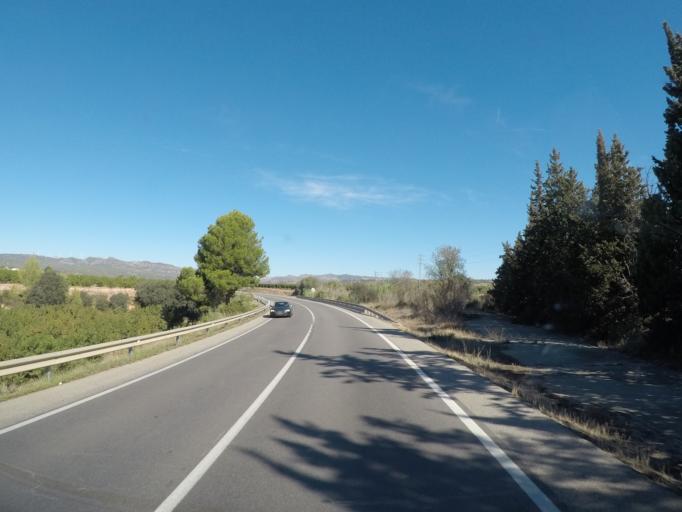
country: ES
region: Catalonia
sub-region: Provincia de Tarragona
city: Garcia
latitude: 41.0859
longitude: 0.6607
